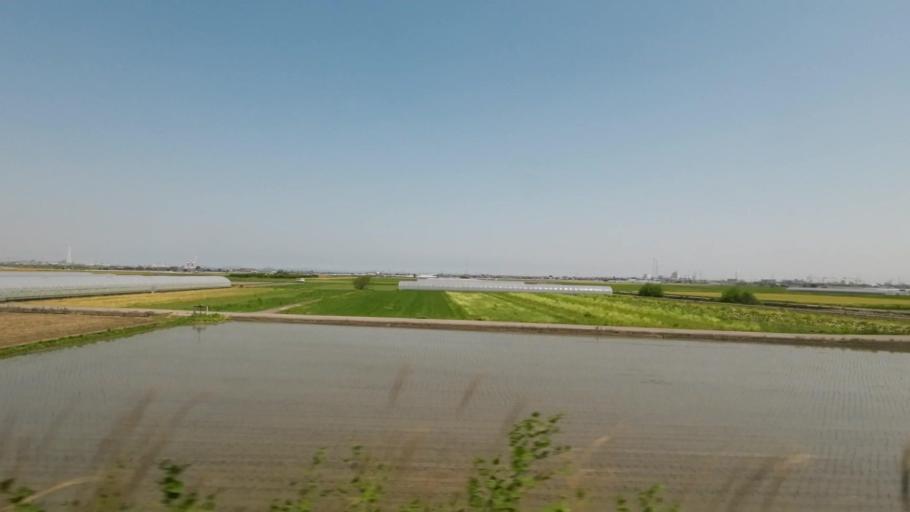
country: JP
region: Ehime
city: Saijo
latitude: 33.8959
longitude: 133.1500
